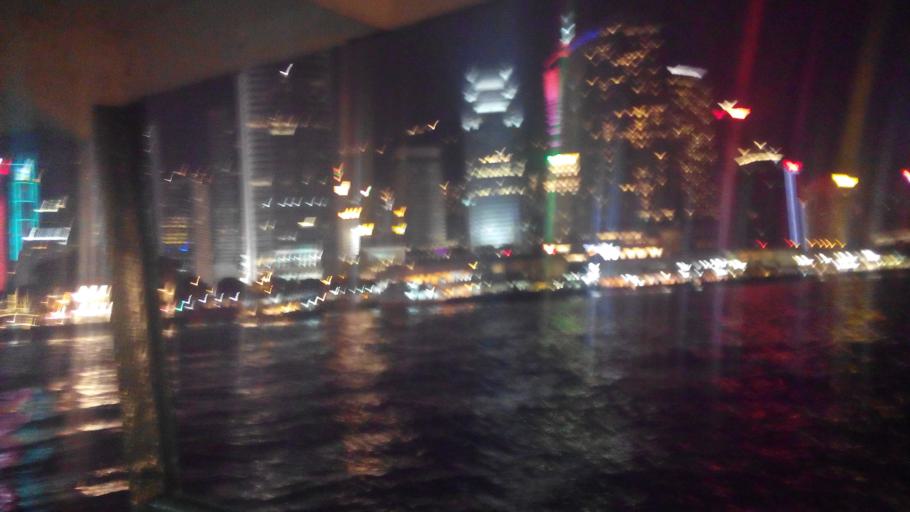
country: HK
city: Hong Kong
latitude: 22.2887
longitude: 114.1620
